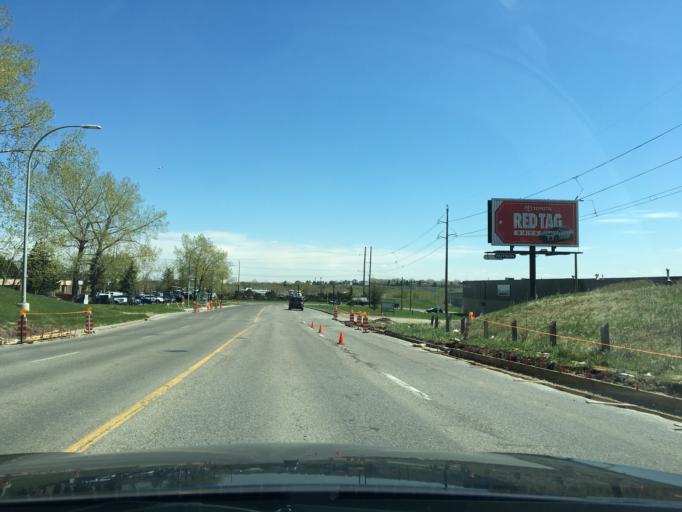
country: CA
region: Alberta
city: Calgary
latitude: 51.0018
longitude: -114.0401
